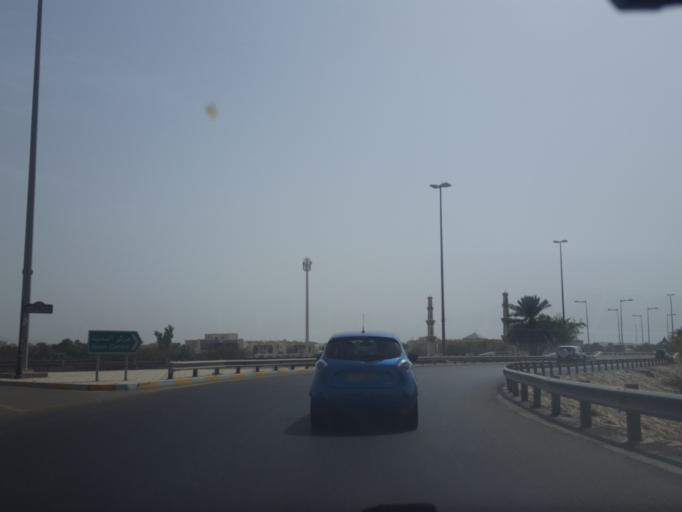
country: OM
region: Al Buraimi
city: Al Buraymi
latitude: 24.2062
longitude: 55.8077
